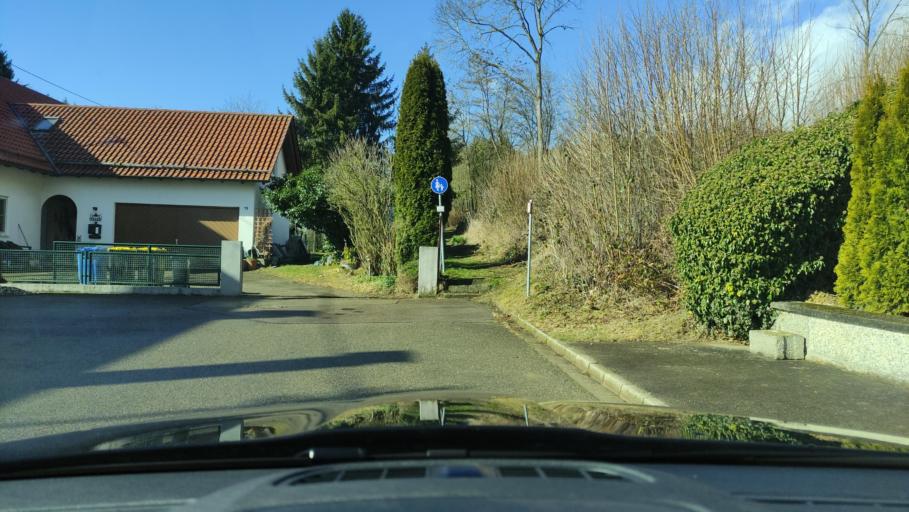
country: DE
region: Bavaria
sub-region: Swabia
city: Krumbach
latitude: 48.2503
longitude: 10.3509
